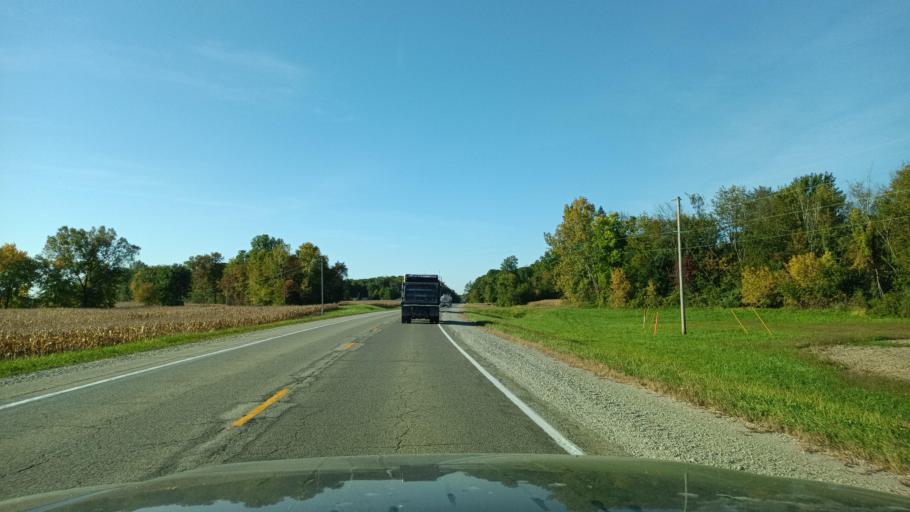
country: US
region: Illinois
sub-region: Clark County
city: Marshall
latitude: 39.4442
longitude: -87.6829
